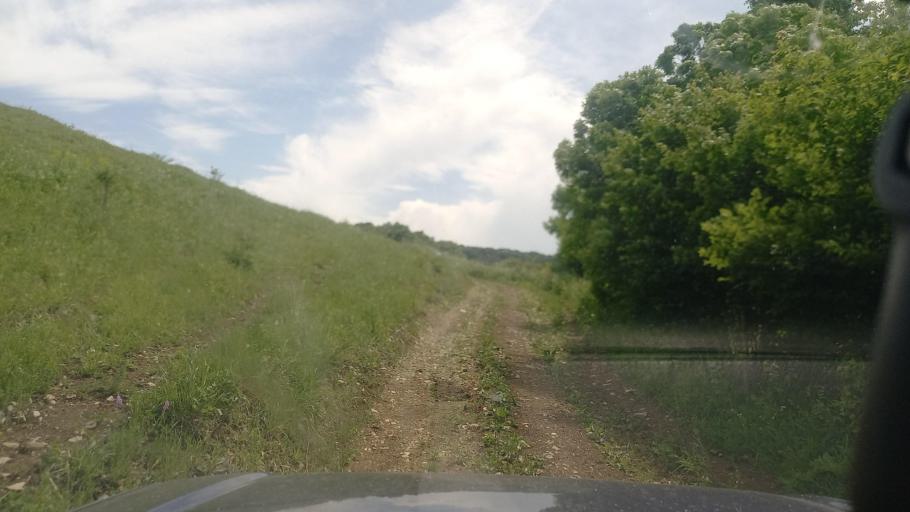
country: RU
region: Karachayevo-Cherkesiya
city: Pregradnaya
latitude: 44.0744
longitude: 41.2831
